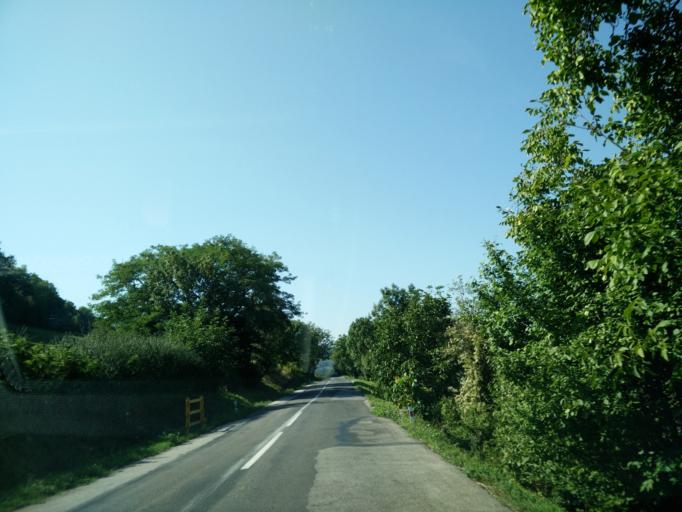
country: SK
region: Nitriansky
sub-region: Okres Nitra
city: Nitra
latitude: 48.3823
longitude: 18.0934
